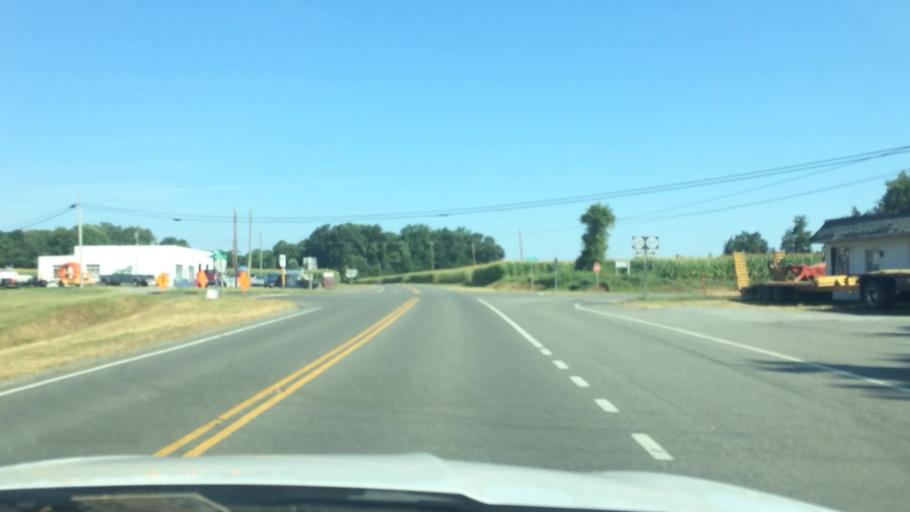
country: US
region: Virginia
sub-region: Lancaster County
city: Lancaster
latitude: 37.7954
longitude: -76.5212
